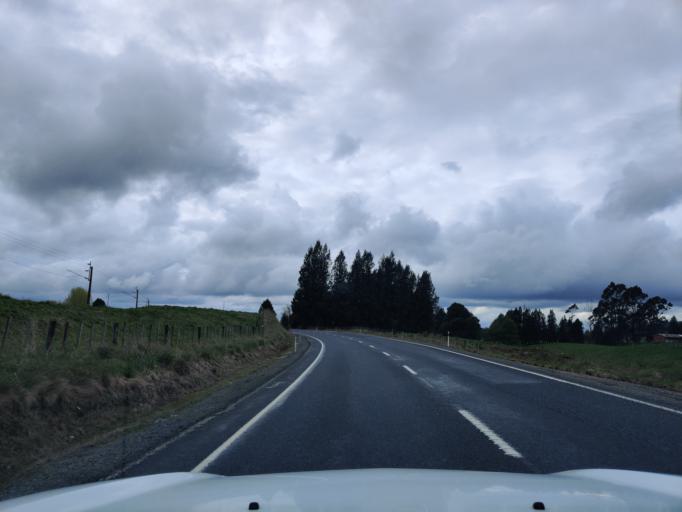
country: NZ
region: Waikato
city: Turangi
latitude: -39.0284
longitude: 175.3824
